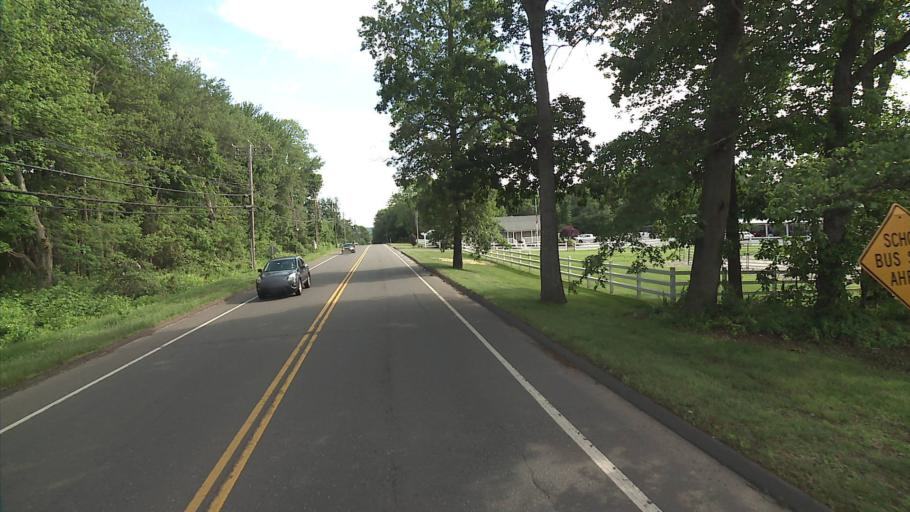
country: US
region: Connecticut
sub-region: New Haven County
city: Prospect
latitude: 41.4420
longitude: -72.9903
